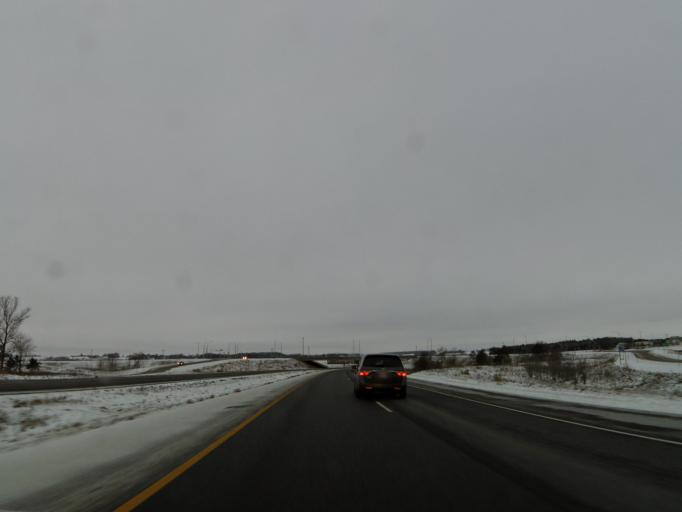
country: US
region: Wisconsin
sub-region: Saint Croix County
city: Baldwin
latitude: 44.9379
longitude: -92.3703
